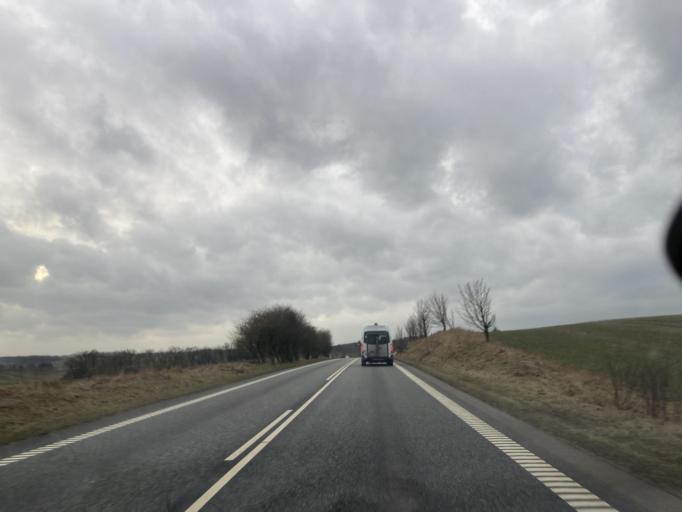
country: DK
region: North Denmark
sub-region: Mariagerfjord Kommune
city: Hobro
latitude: 56.6155
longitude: 9.6627
